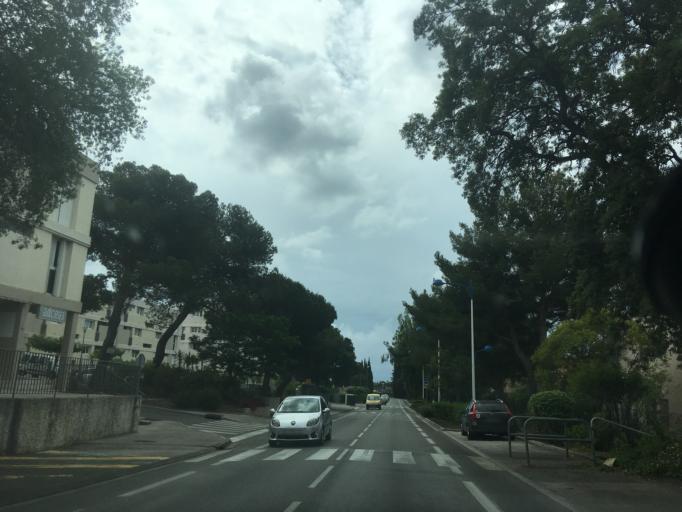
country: FR
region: Provence-Alpes-Cote d'Azur
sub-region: Departement du Var
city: La Londe-les-Maures
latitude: 43.1313
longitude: 6.2392
